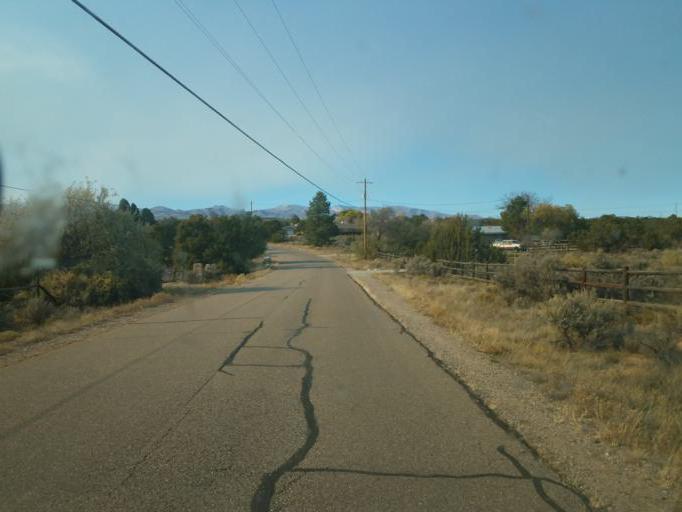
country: US
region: New Mexico
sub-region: Los Alamos County
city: White Rock
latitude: 35.8093
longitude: -106.2218
